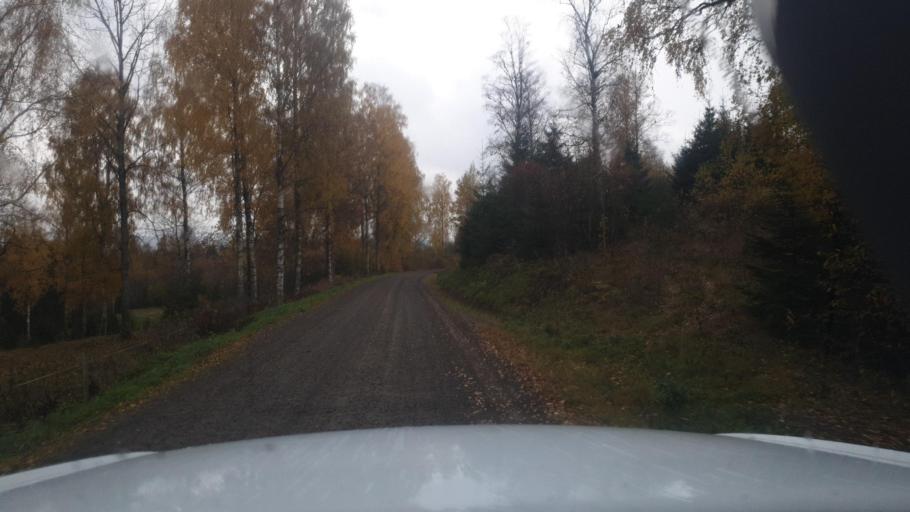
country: SE
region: Vaermland
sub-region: Torsby Kommun
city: Torsby
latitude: 59.9750
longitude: 12.8559
